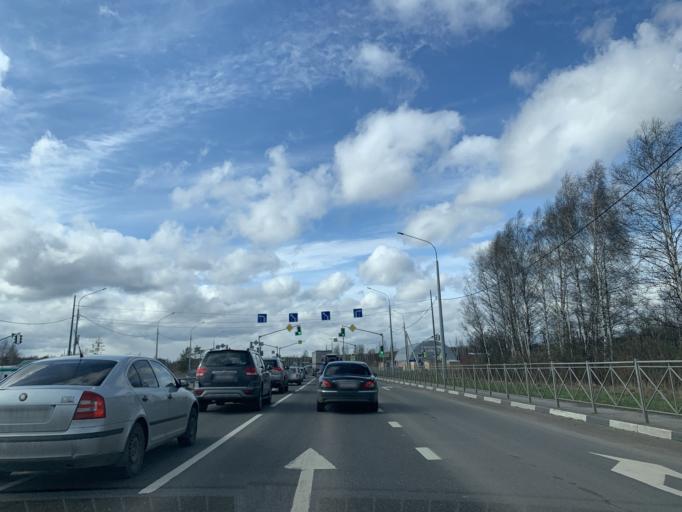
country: RU
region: Jaroslavl
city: Yaroslavl
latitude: 57.6703
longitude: 39.9472
